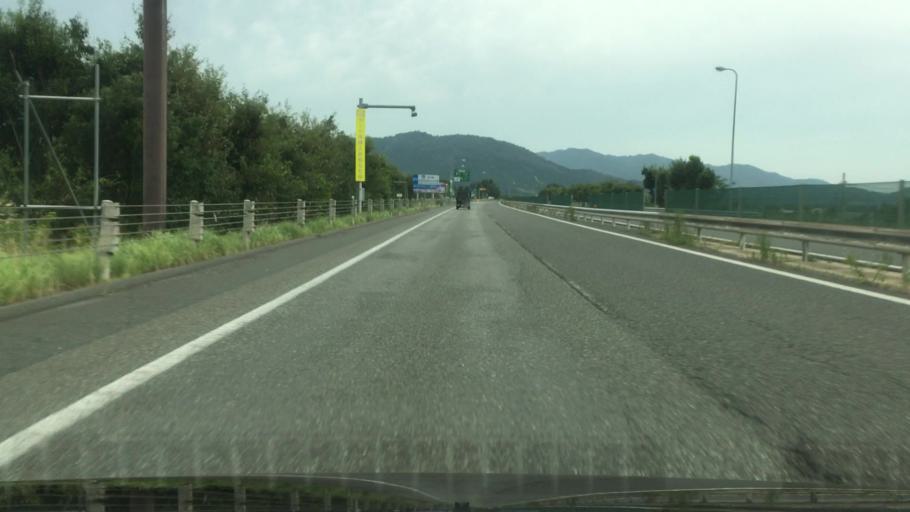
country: JP
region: Hyogo
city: Sasayama
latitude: 35.1600
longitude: 135.1198
